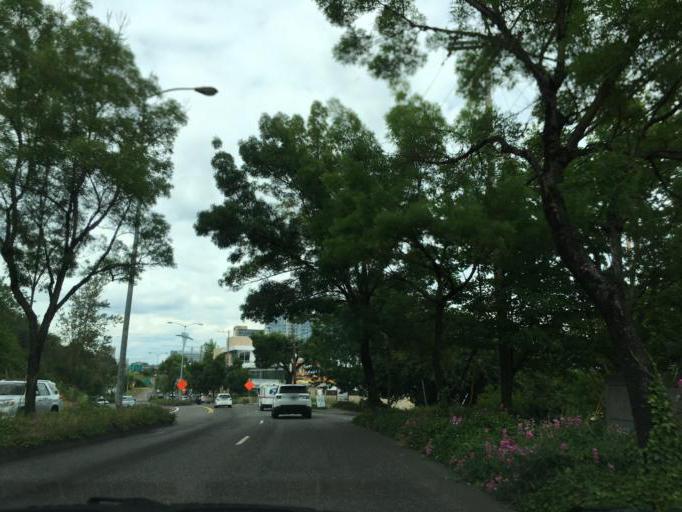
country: US
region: Oregon
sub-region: Multnomah County
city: Portland
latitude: 45.4912
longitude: -122.6731
